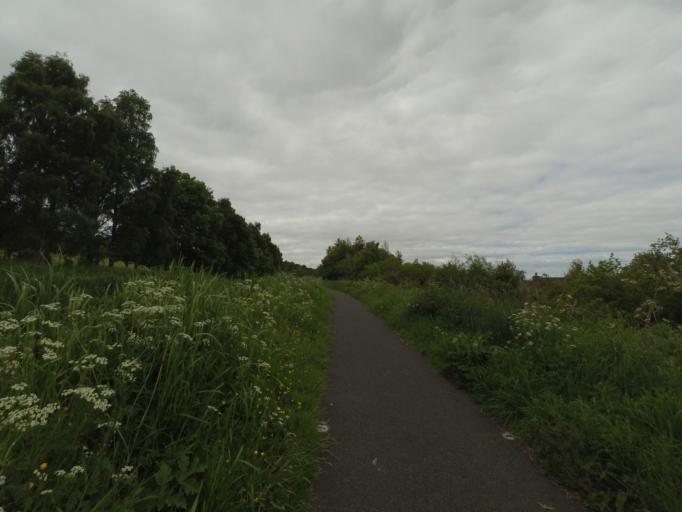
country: GB
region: Scotland
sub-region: West Lothian
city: Linlithgow
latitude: 55.9677
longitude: -3.6181
